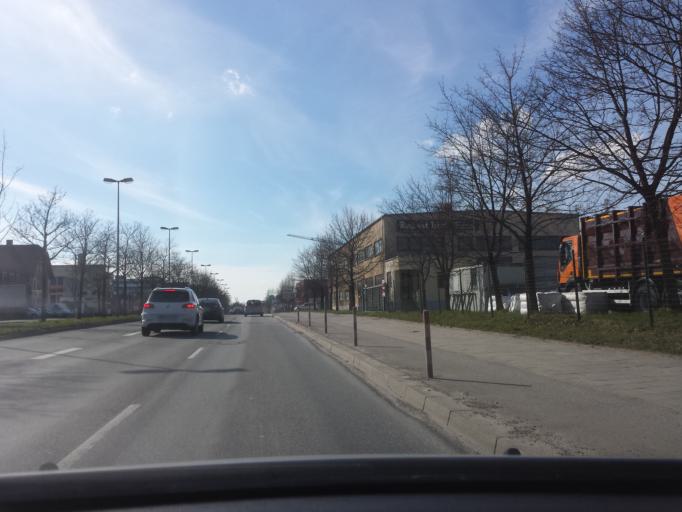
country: DE
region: Bavaria
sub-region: Upper Bavaria
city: Munich
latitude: 48.1868
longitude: 11.5387
